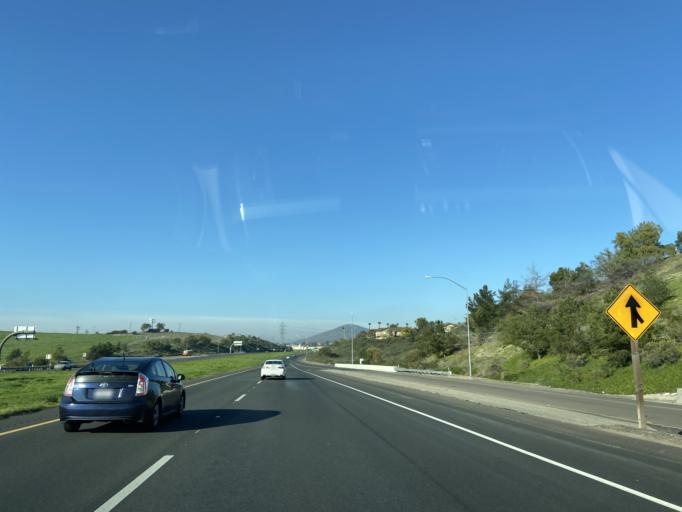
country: US
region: California
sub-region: San Diego County
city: Bonita
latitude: 32.6333
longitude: -116.9711
